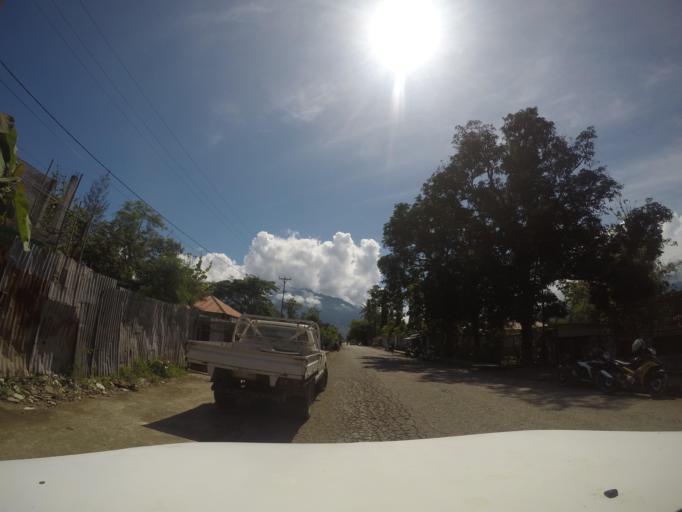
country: TL
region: Bobonaro
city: Maliana
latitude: -8.9906
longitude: 125.2010
